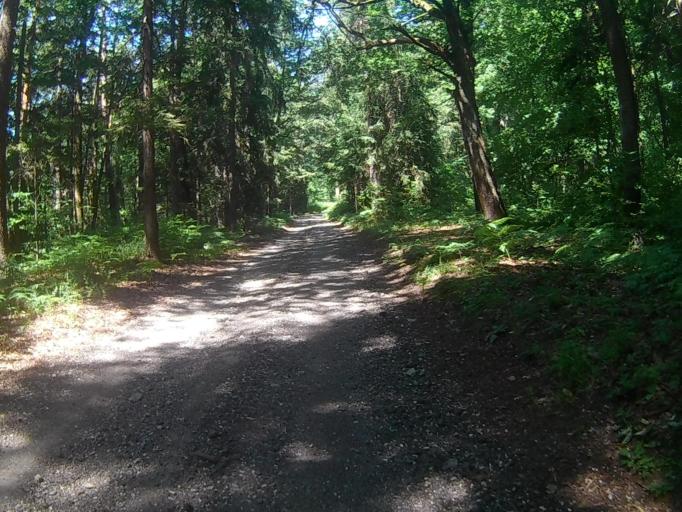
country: SI
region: Race-Fram
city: Fram
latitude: 46.4722
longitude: 15.6280
